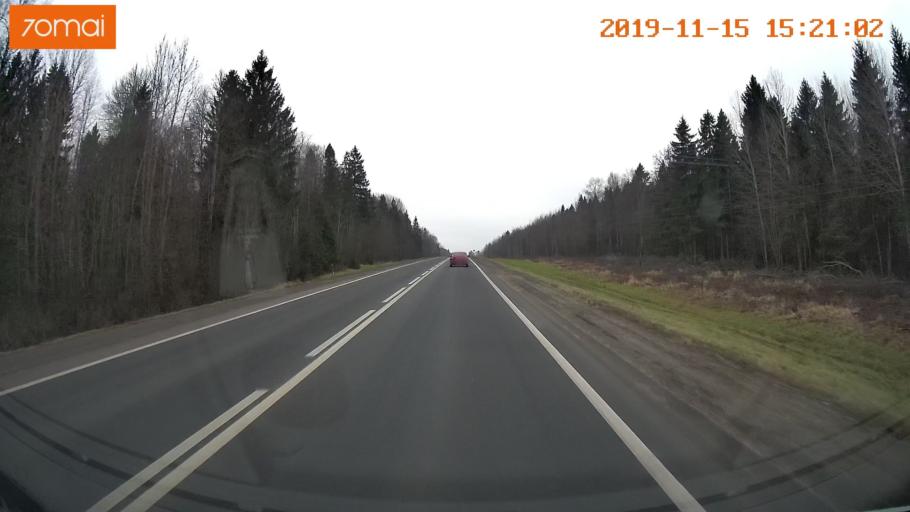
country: RU
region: Jaroslavl
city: Danilov
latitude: 58.2170
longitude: 40.1521
